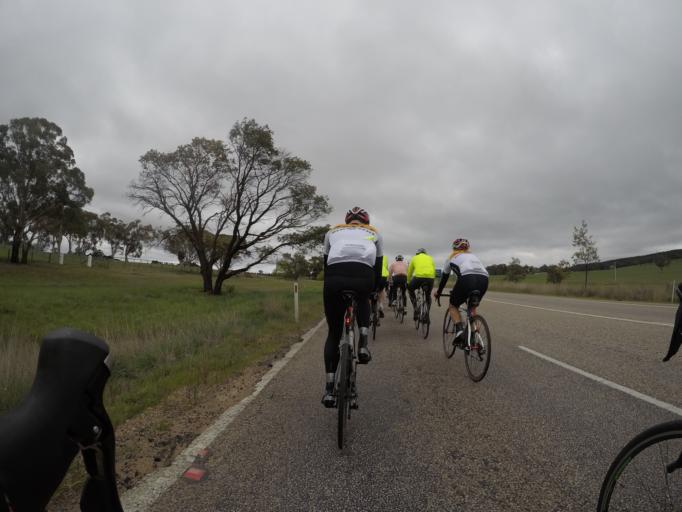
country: AU
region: New South Wales
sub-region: Lithgow
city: Portland
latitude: -33.4332
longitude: 149.9029
